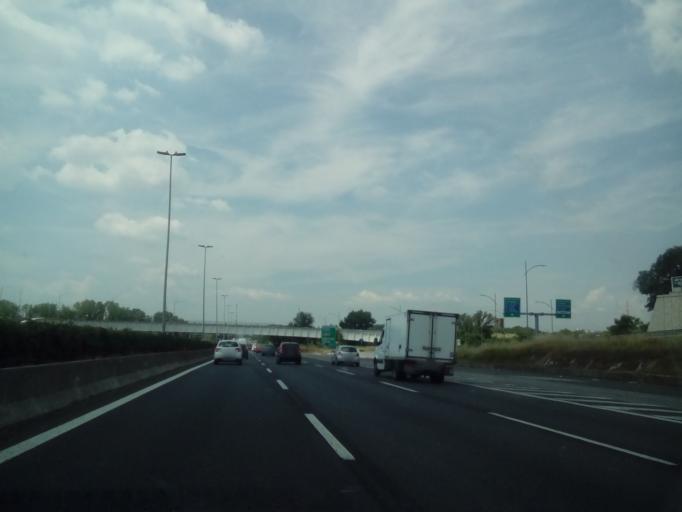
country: IT
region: Latium
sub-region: Citta metropolitana di Roma Capitale
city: Setteville
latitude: 41.9217
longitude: 12.6107
